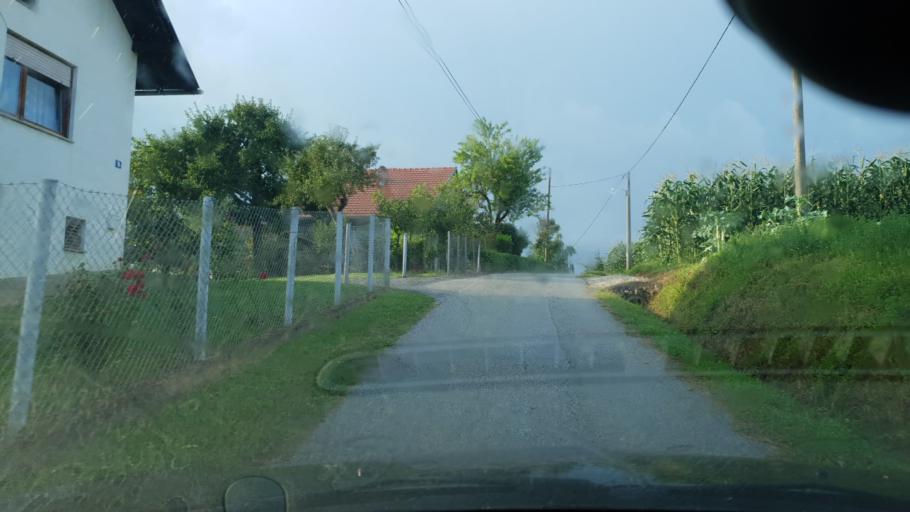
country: HR
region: Krapinsko-Zagorska
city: Zabok
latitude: 46.0936
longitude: 15.9120
